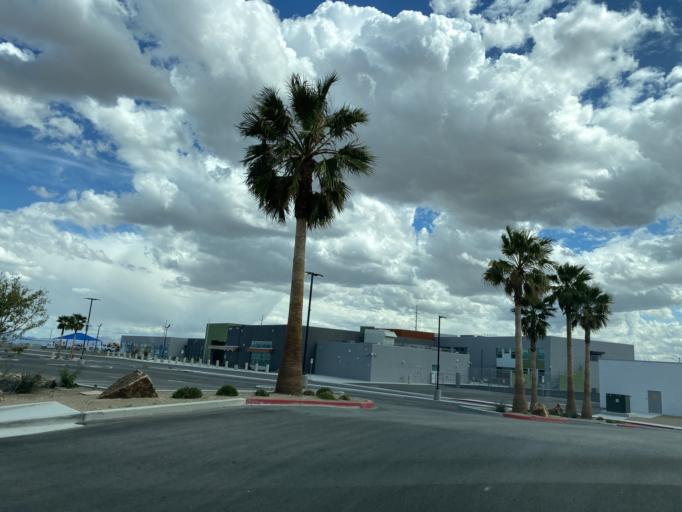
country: US
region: Nevada
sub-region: Clark County
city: Summerlin South
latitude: 36.3011
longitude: -115.3110
